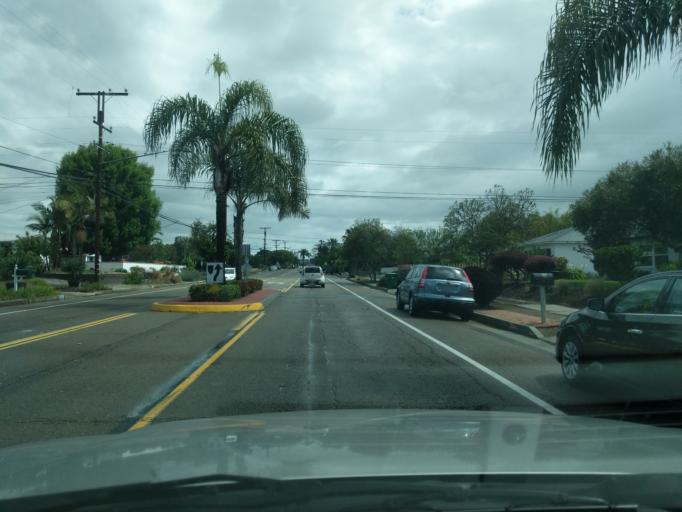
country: US
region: California
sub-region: San Diego County
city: Carlsbad
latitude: 33.1734
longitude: -117.3574
